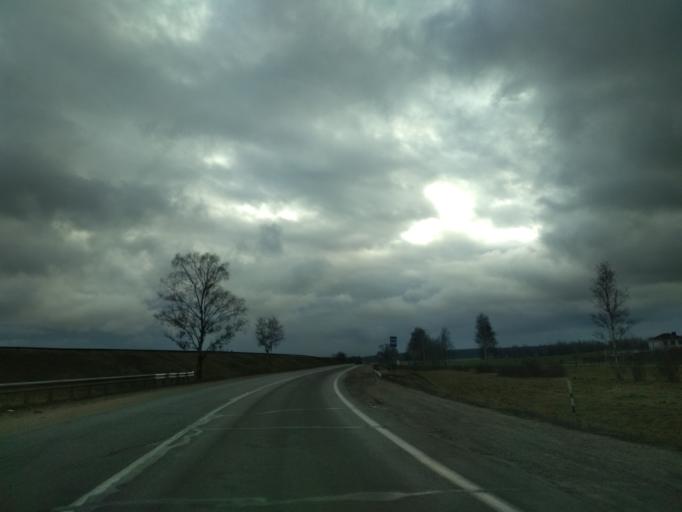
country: BY
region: Minsk
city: Pryvol'ny
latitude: 53.7922
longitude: 27.8183
